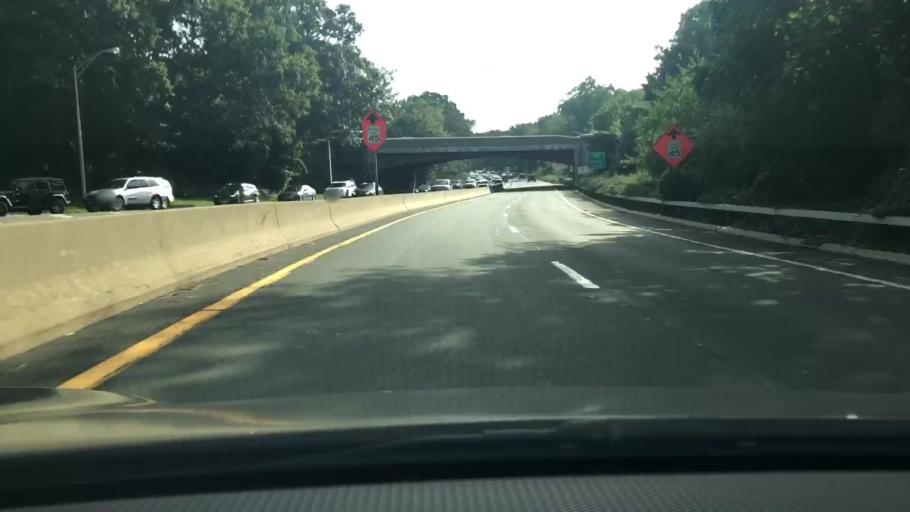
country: US
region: New York
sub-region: Westchester County
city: Pelham
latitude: 40.9225
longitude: -73.8091
